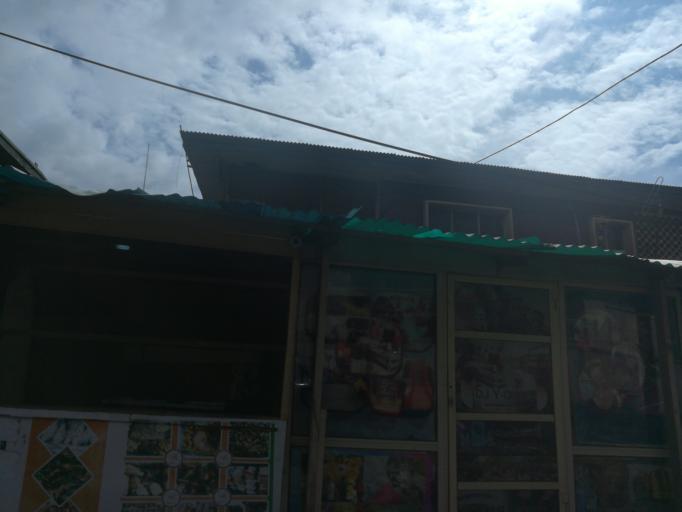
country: NG
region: Lagos
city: Somolu
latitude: 6.5482
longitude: 3.3743
